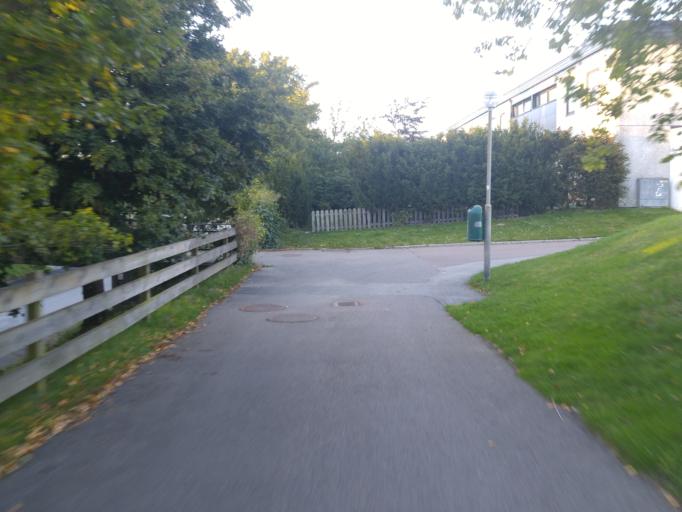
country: SE
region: Skane
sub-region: Lunds Kommun
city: Lund
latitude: 55.7268
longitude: 13.2000
